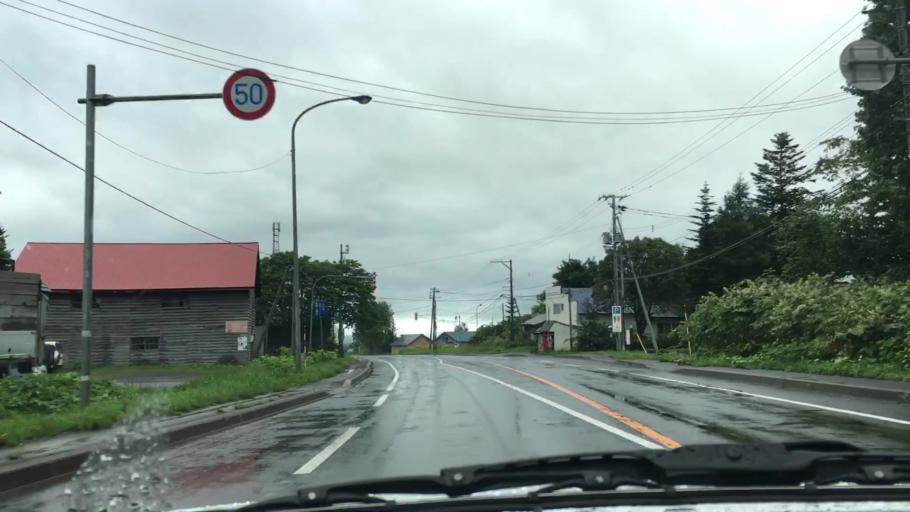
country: JP
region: Hokkaido
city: Niseko Town
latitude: 42.6953
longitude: 140.8403
